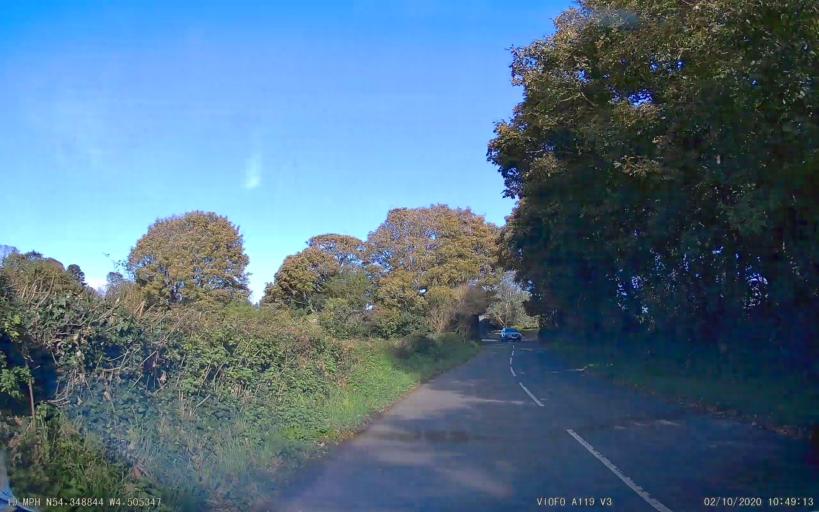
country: IM
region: Ramsey
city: Ramsey
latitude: 54.3488
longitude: -4.5053
